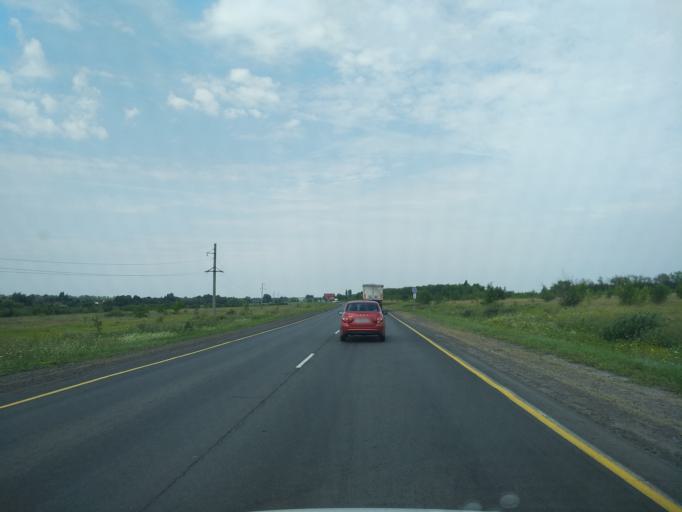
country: RU
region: Voronezj
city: Orlovo
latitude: 51.6795
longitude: 39.6628
